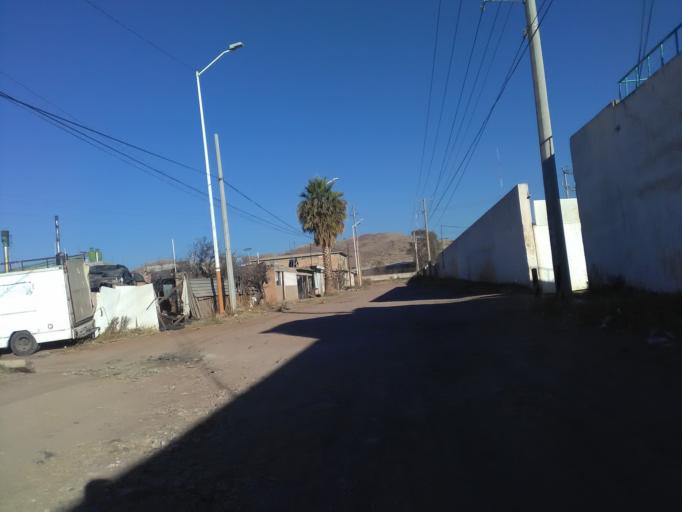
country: MX
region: Durango
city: Victoria de Durango
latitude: 24.0558
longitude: -104.6539
